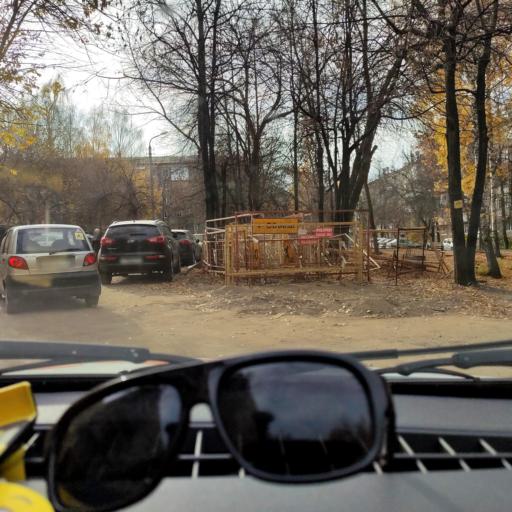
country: RU
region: Bashkortostan
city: Ufa
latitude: 54.7456
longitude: 56.0224
